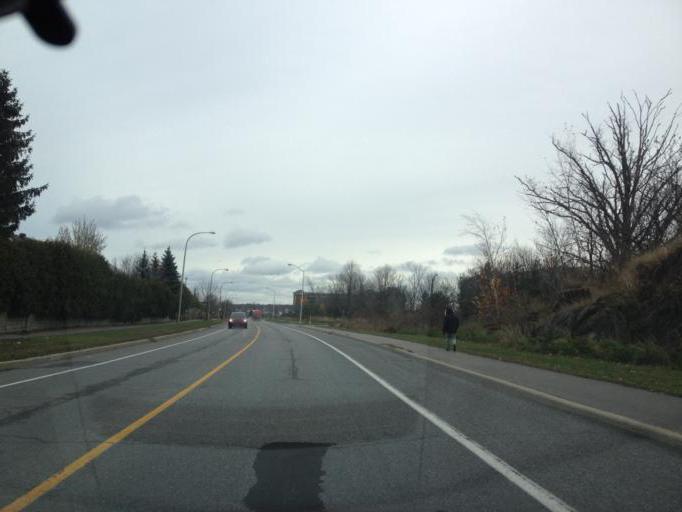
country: CA
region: Ontario
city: Bells Corners
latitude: 45.3154
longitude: -75.9063
